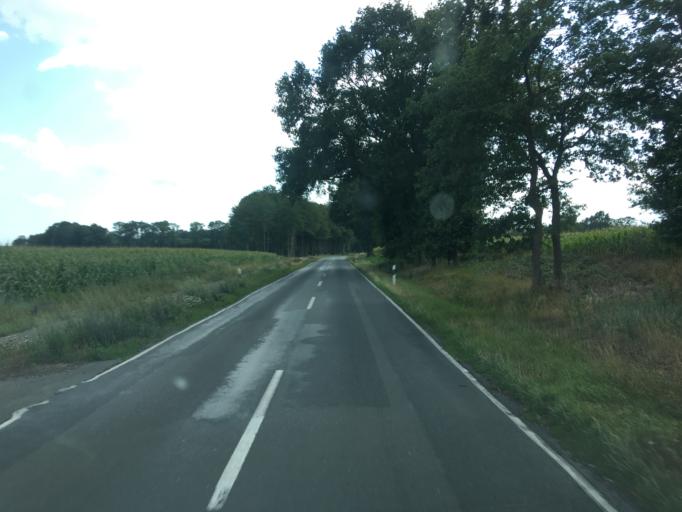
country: DE
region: Lower Saxony
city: Friesoythe
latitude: 53.0487
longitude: 7.8577
